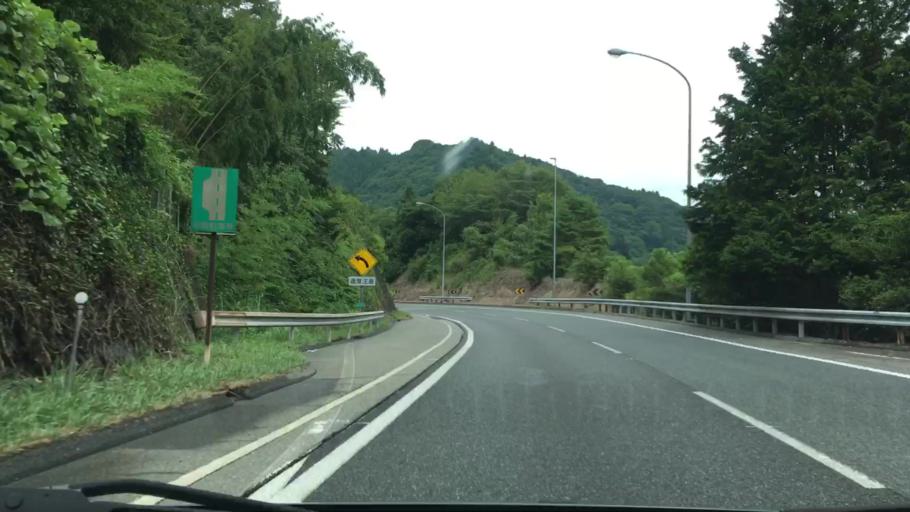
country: JP
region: Okayama
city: Niimi
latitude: 34.9854
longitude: 133.6112
